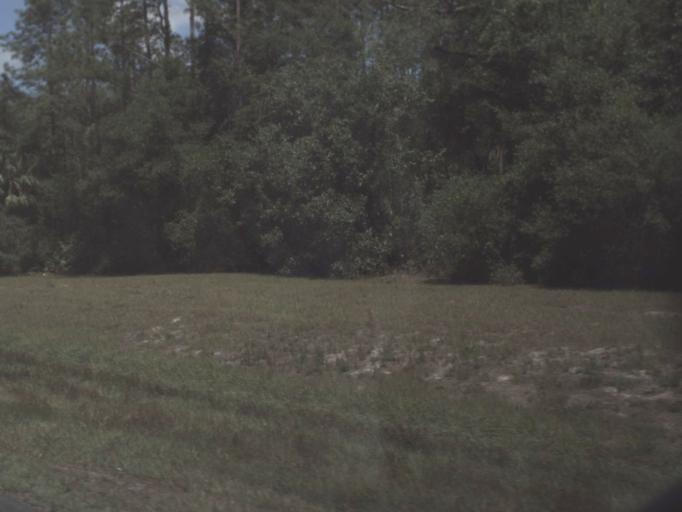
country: US
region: Florida
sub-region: Marion County
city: Ocala
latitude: 29.2191
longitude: -82.0316
